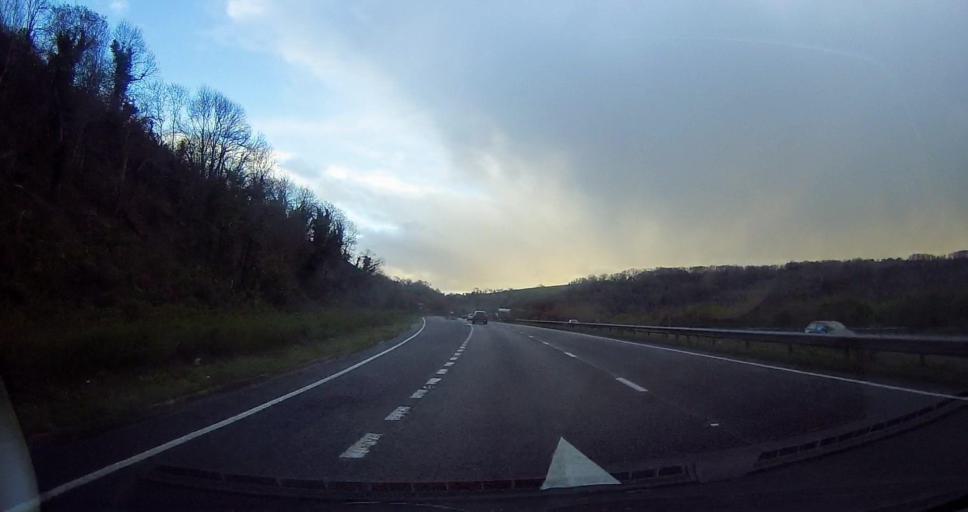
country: GB
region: England
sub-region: West Sussex
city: Hurstpierpoint
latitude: 50.9081
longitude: -0.1896
